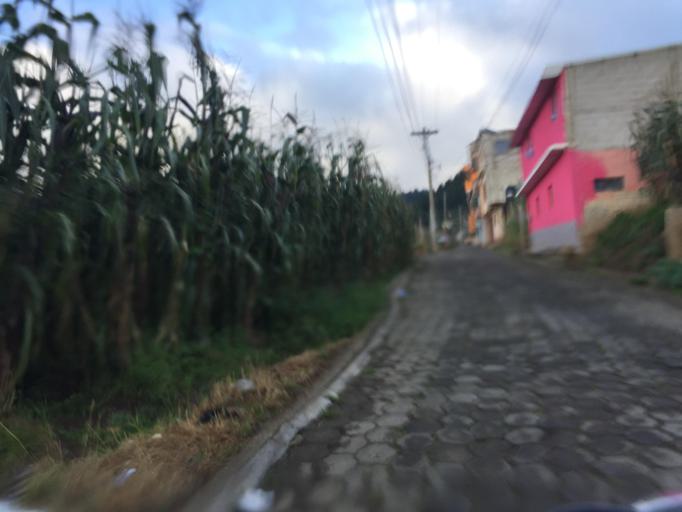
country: GT
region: Totonicapan
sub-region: Municipio de Totonicapan
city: Totonicapan
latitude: 14.9135
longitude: -91.3554
